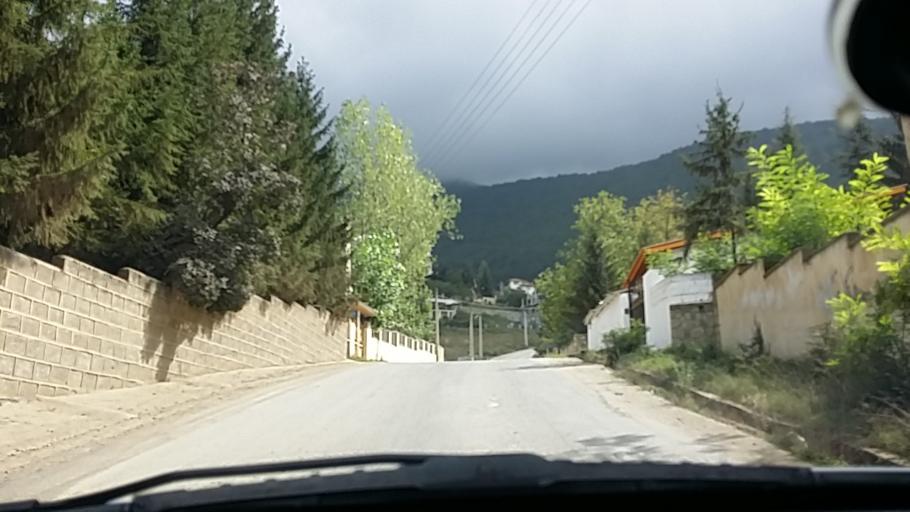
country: IR
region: Mazandaran
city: `Abbasabad
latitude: 36.4961
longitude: 51.1651
